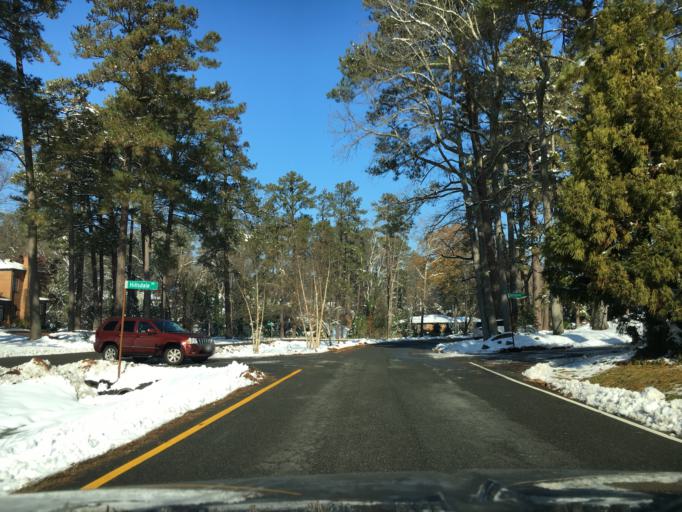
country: US
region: Virginia
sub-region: Henrico County
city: Tuckahoe
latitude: 37.5810
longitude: -77.5499
